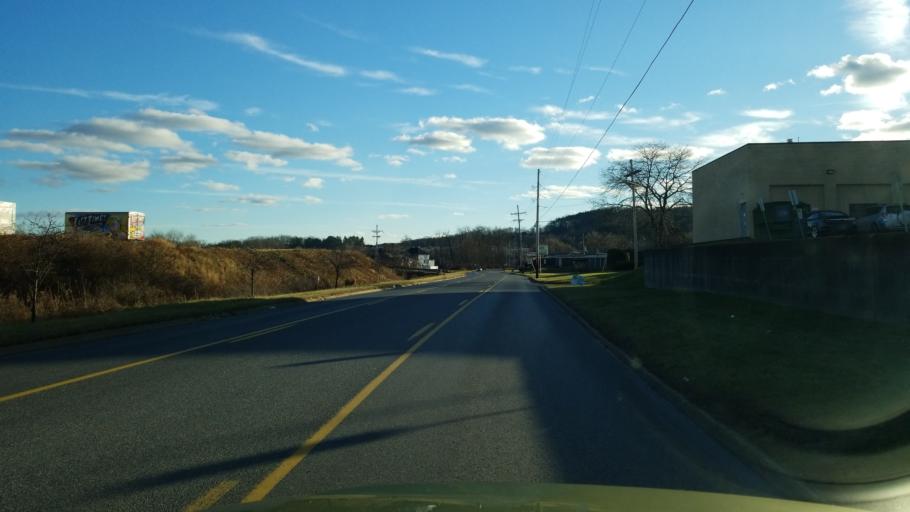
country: US
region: Pennsylvania
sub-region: Indiana County
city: Indiana
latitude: 40.6211
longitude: -79.1891
